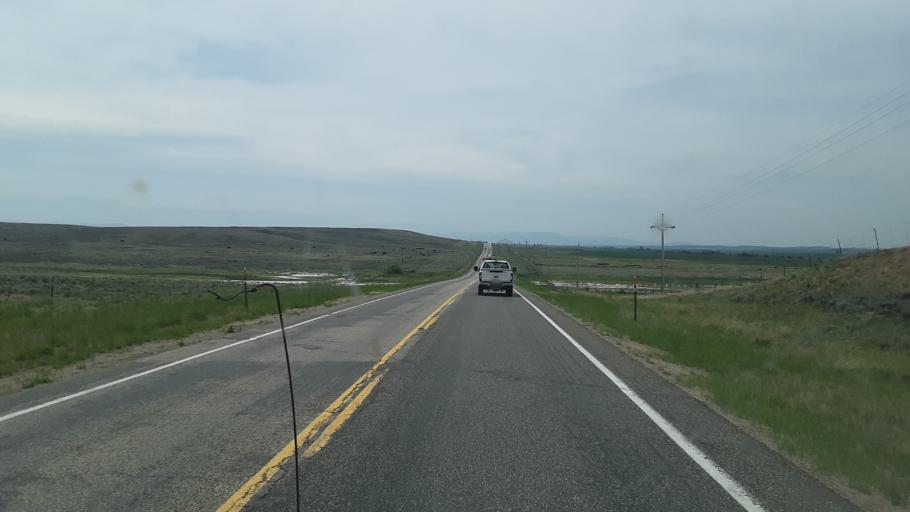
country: US
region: Colorado
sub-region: Jackson County
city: Walden
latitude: 40.7850
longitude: -106.2813
